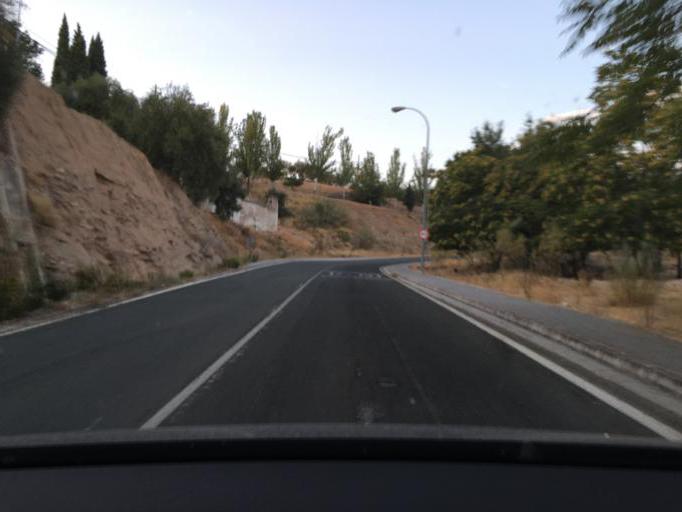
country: ES
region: Andalusia
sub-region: Provincia de Granada
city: Viznar
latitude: 37.2063
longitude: -3.5588
